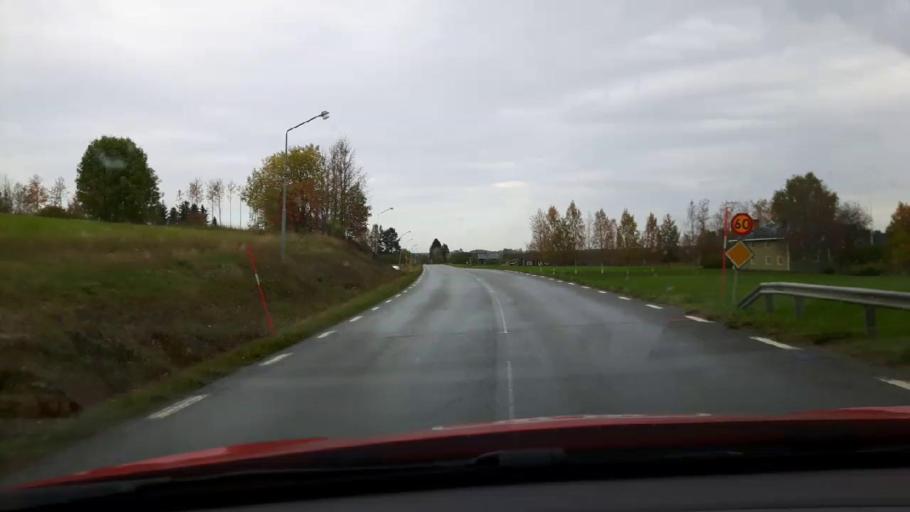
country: SE
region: Jaemtland
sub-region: Bergs Kommun
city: Hoverberg
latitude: 63.0153
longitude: 14.3439
